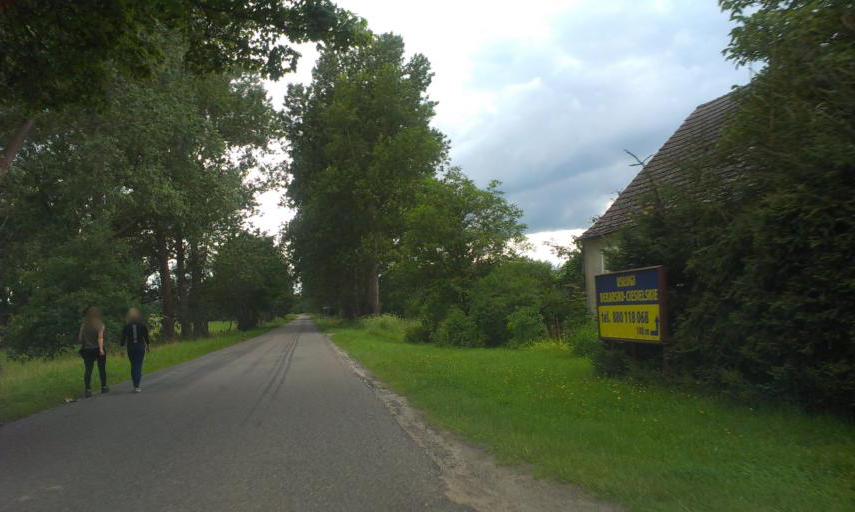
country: PL
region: West Pomeranian Voivodeship
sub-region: Powiat bialogardzki
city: Tychowo
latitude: 53.8921
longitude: 16.1983
